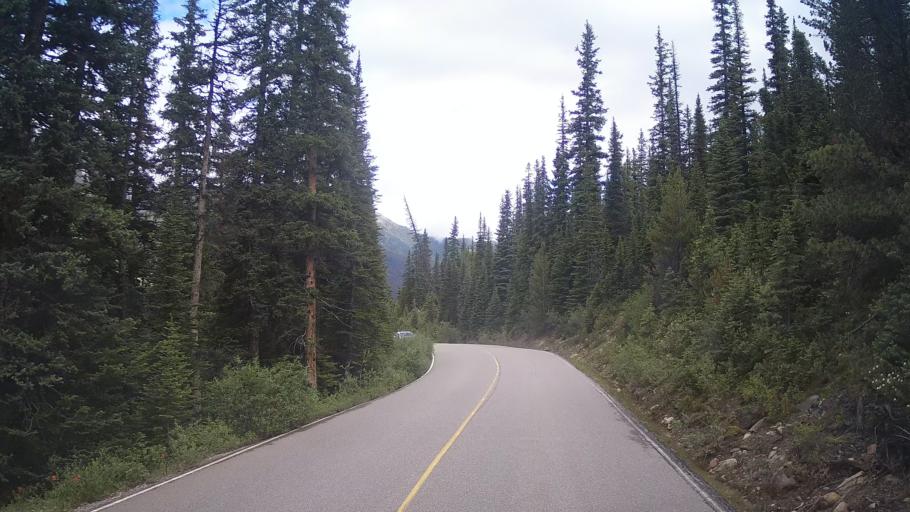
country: CA
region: Alberta
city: Jasper Park Lodge
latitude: 52.6985
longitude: -118.0586
